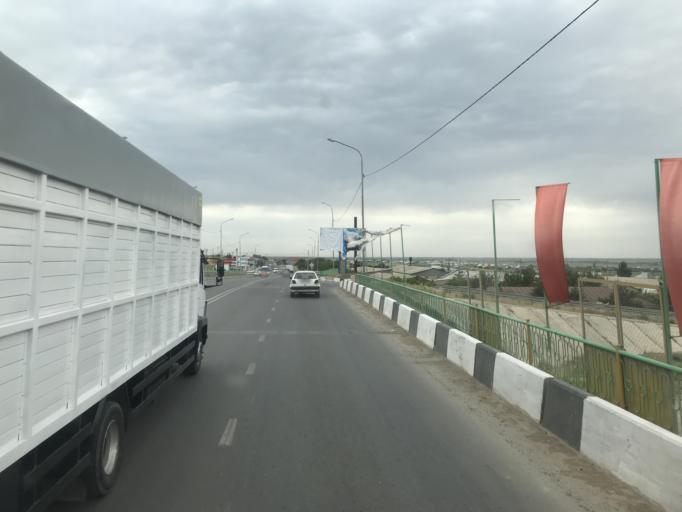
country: KZ
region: Ongtustik Qazaqstan
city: Saryaghash
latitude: 41.4603
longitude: 69.1473
